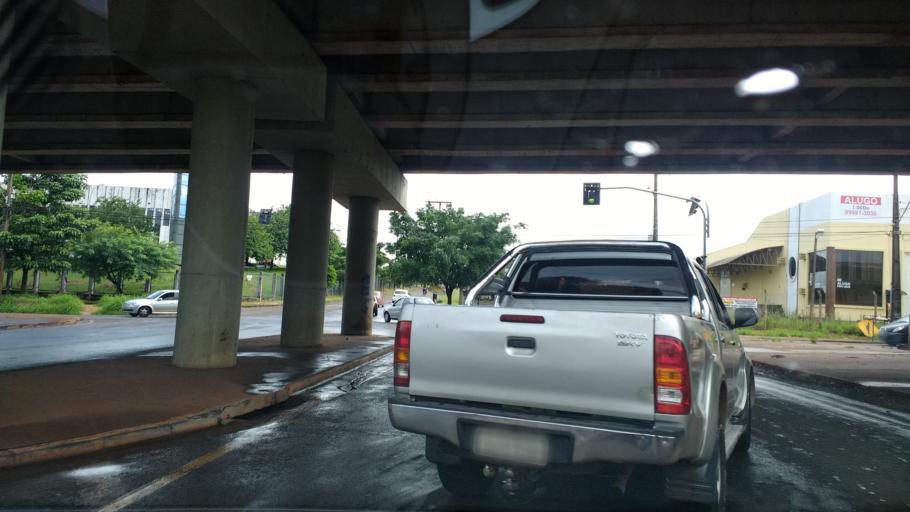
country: BR
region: Parana
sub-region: Londrina
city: Londrina
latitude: -23.3169
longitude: -51.2112
